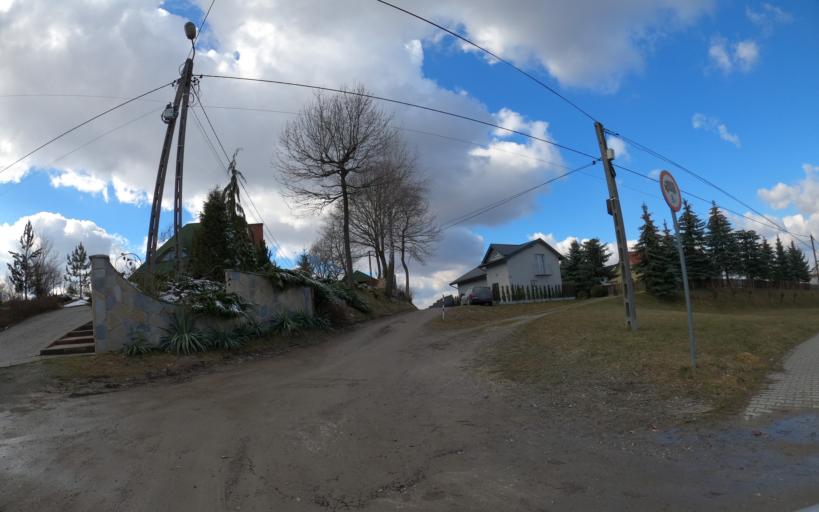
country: PL
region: Subcarpathian Voivodeship
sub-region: Powiat debicki
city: Debica
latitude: 50.0311
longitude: 21.4414
